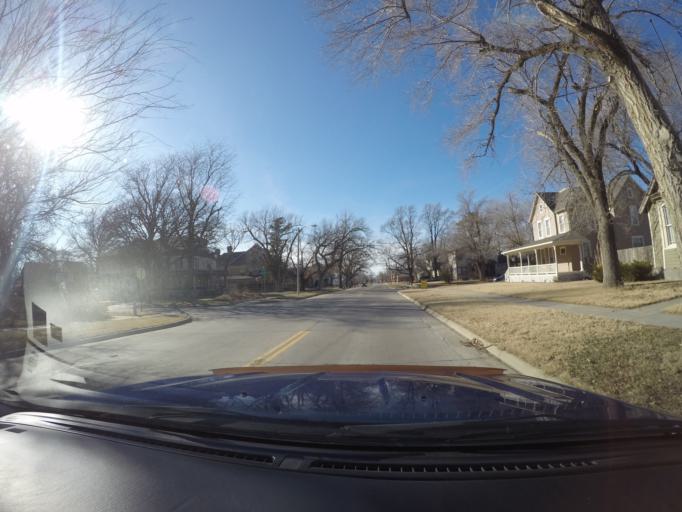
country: US
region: Kansas
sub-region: Harvey County
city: Newton
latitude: 38.0428
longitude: -97.3426
